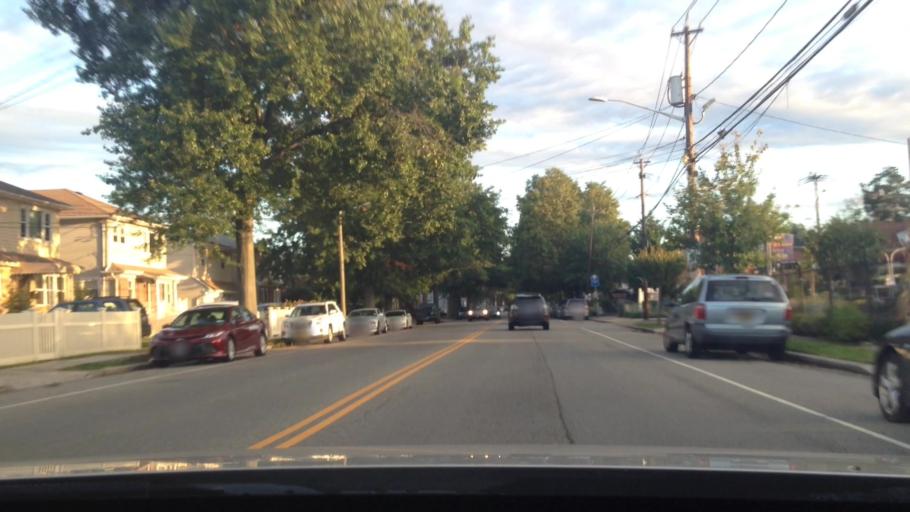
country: US
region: New York
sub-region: Nassau County
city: Garden City South
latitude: 40.7096
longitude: -73.6611
